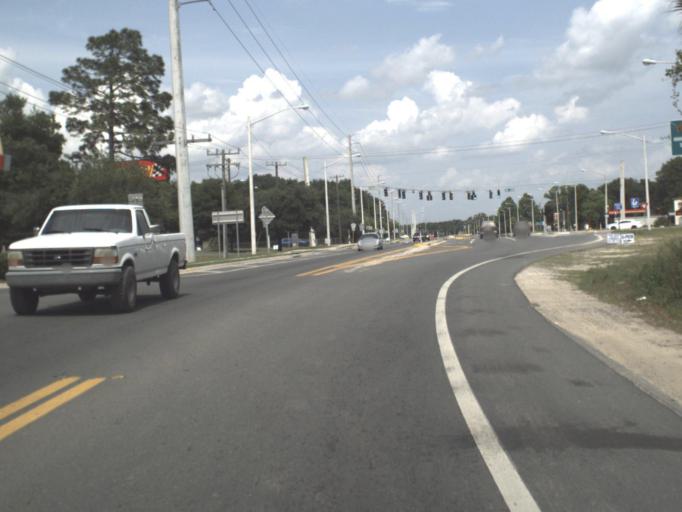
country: US
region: Florida
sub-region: Putnam County
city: Interlachen
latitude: 29.6277
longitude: -81.8881
